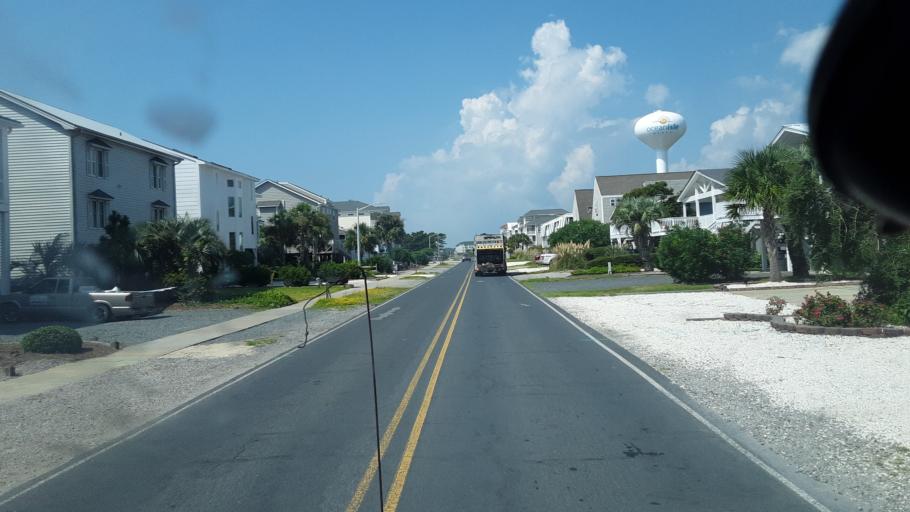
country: US
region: North Carolina
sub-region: Brunswick County
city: Sunset Beach
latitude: 33.8835
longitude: -78.4527
